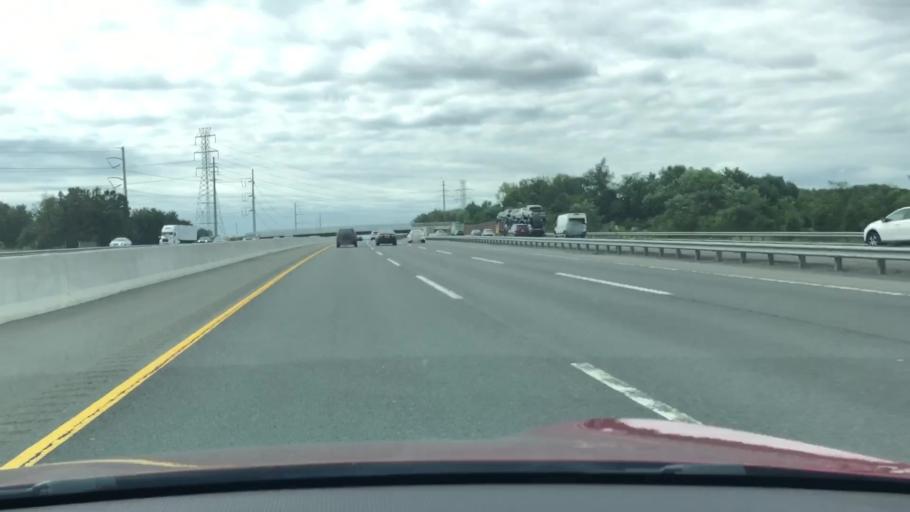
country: US
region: New Jersey
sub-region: Mercer County
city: Hightstown
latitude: 40.2420
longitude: -74.5282
